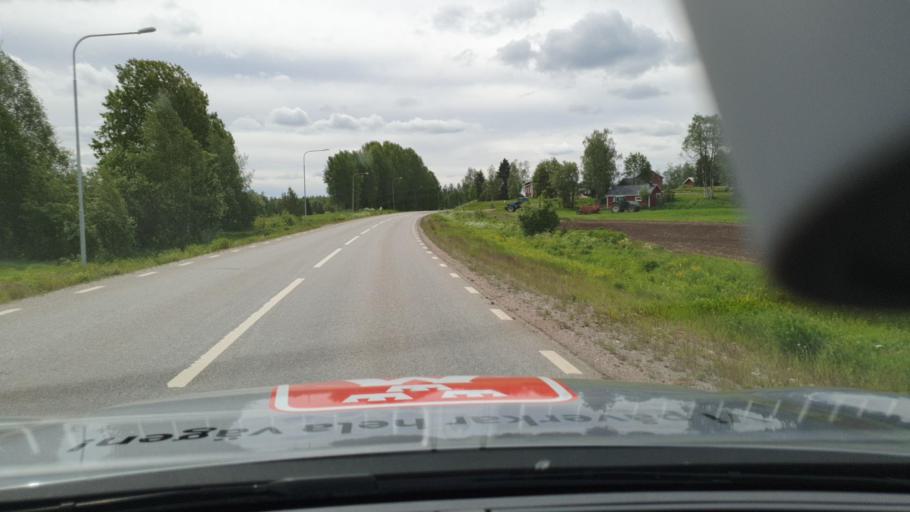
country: SE
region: Norrbotten
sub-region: Kalix Kommun
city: Kalix
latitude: 65.9714
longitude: 23.4609
